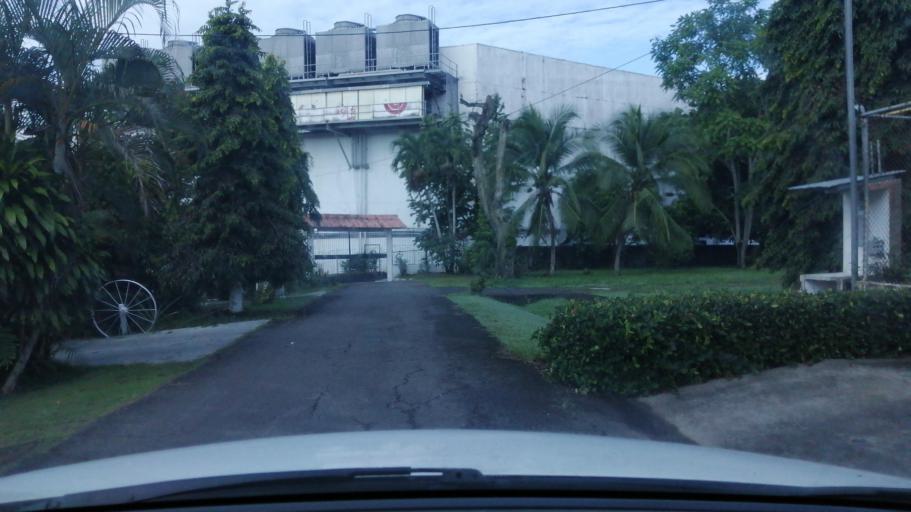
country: PA
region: Chiriqui
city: Mata del Nance
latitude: 8.4465
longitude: -82.4189
